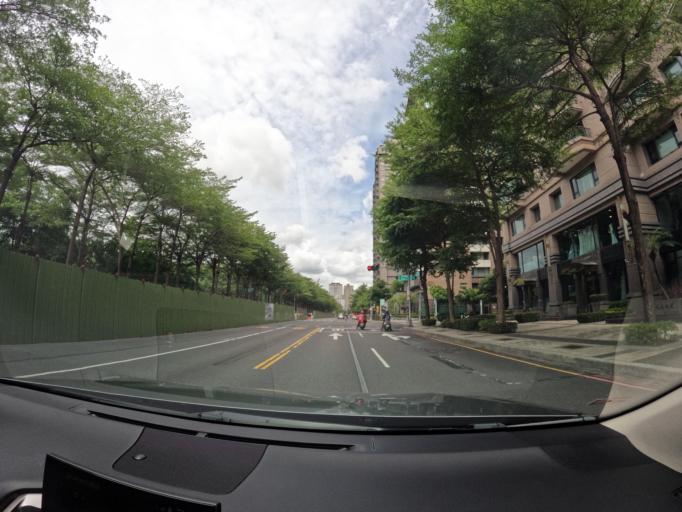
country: TW
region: Kaohsiung
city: Kaohsiung
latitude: 22.6549
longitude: 120.2845
